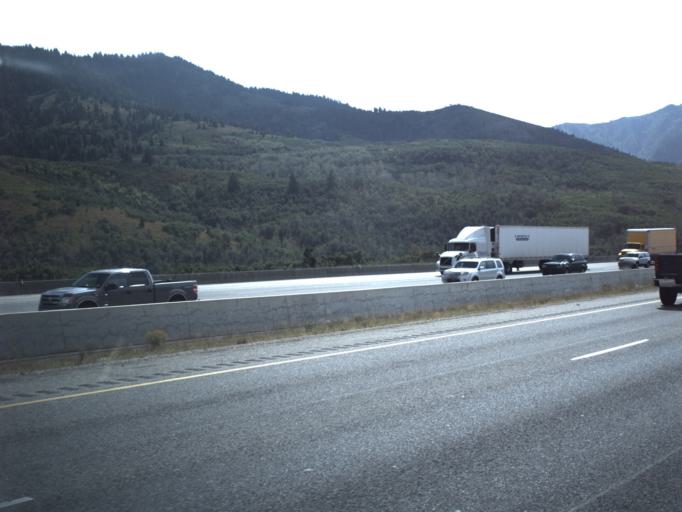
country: US
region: Utah
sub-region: Summit County
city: Summit Park
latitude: 40.7486
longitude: -111.6360
